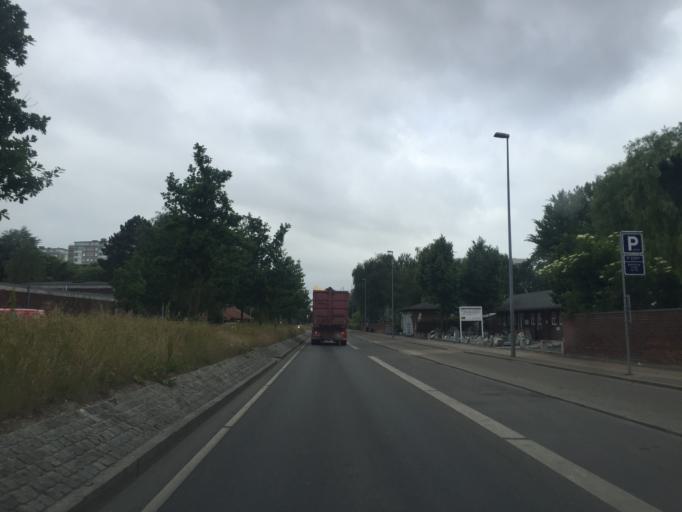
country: DK
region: Capital Region
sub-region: Frederiksberg Kommune
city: Frederiksberg
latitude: 55.6722
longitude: 12.5119
